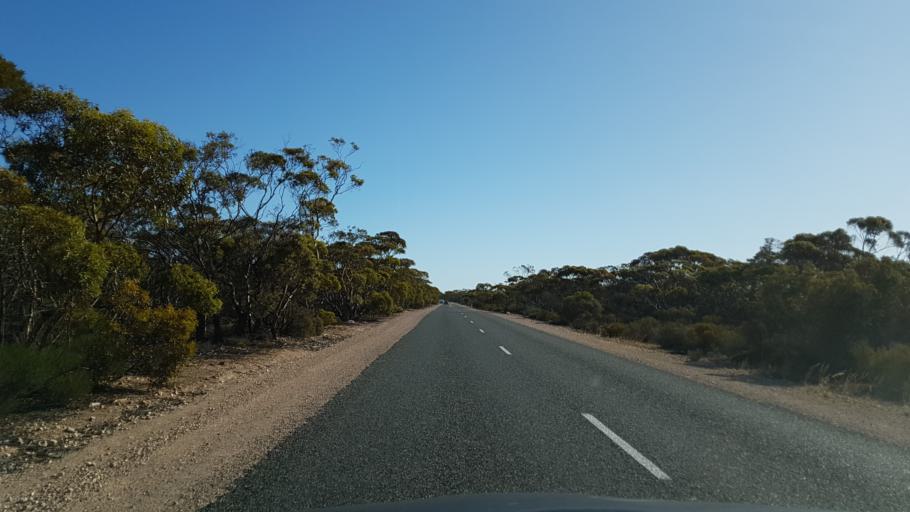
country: AU
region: South Australia
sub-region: Mid Murray
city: Mannum
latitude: -34.7936
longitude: 139.5072
